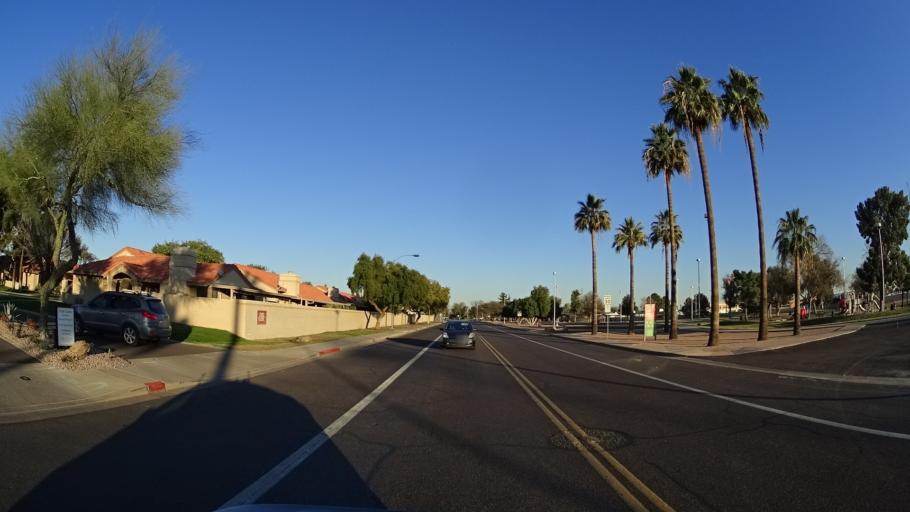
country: US
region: Arizona
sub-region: Maricopa County
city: Mesa
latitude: 33.4296
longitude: -111.8270
